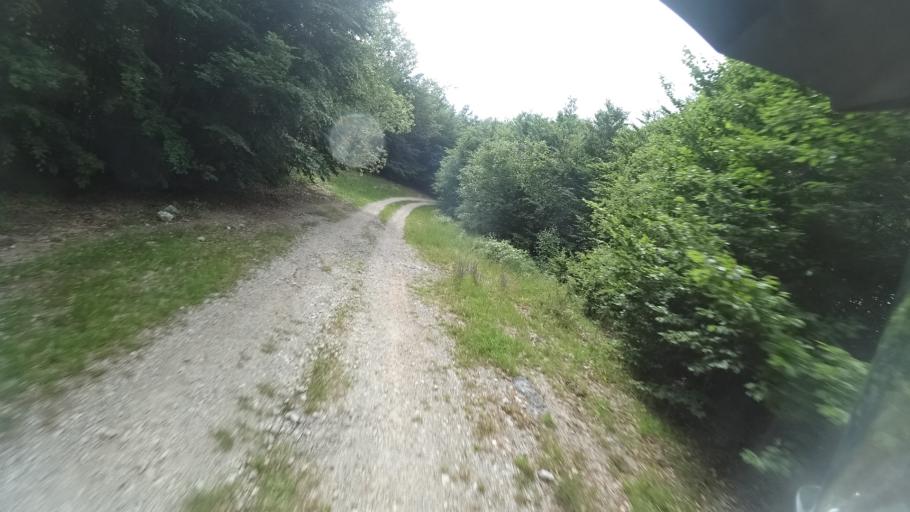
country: HR
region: Zadarska
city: Obrovac
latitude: 44.2823
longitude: 15.7143
